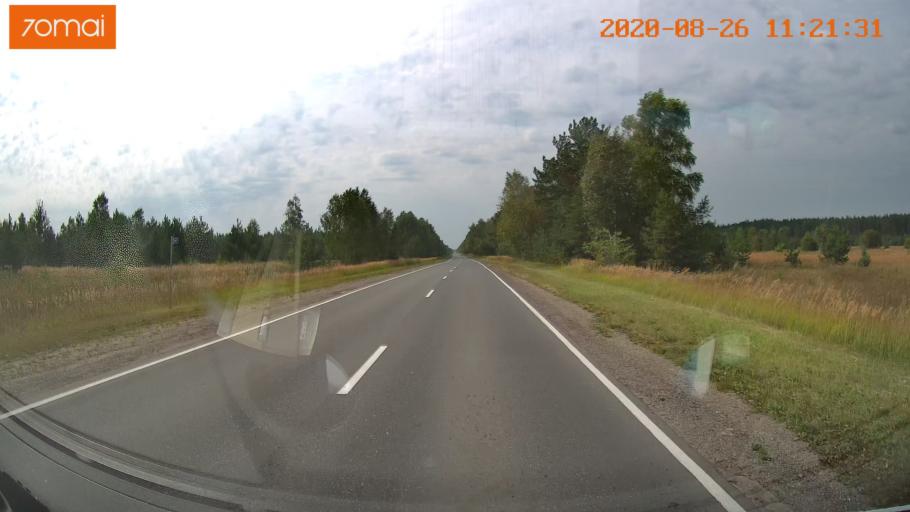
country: RU
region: Rjazan
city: Shilovo
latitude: 54.3752
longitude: 41.0433
